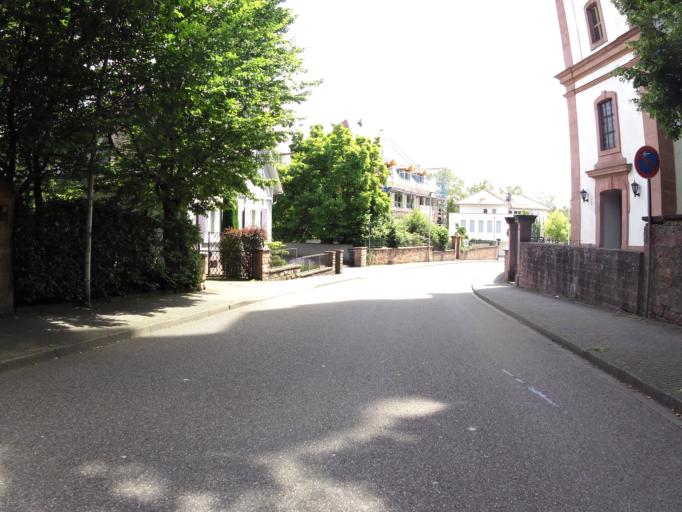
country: DE
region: Baden-Wuerttemberg
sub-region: Freiburg Region
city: Lahr
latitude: 48.3406
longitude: 7.8554
